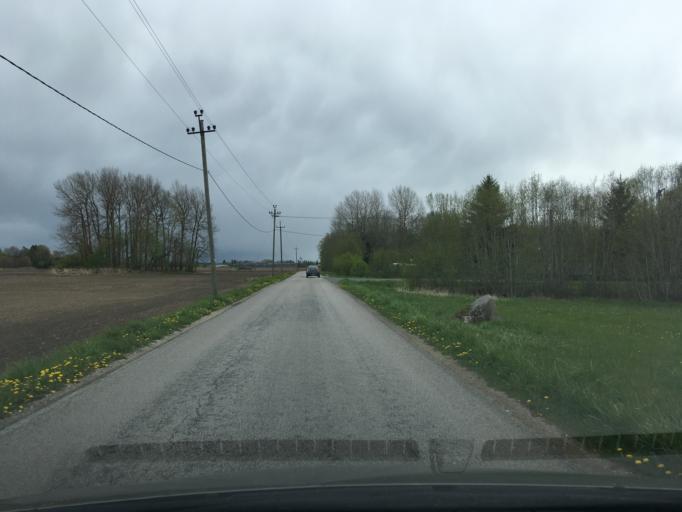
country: EE
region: Harju
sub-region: Joelaehtme vald
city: Loo
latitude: 59.3773
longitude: 24.9661
